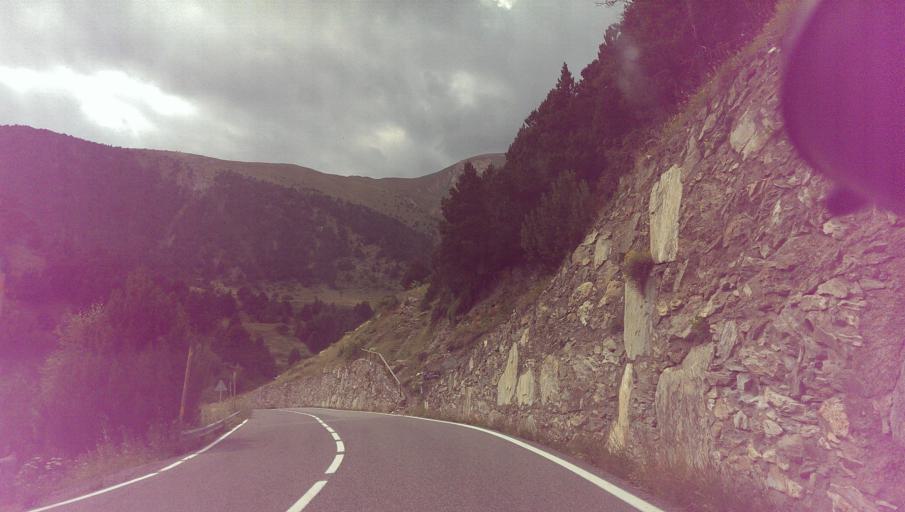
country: AD
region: Canillo
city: Canillo
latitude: 42.5727
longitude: 1.5924
